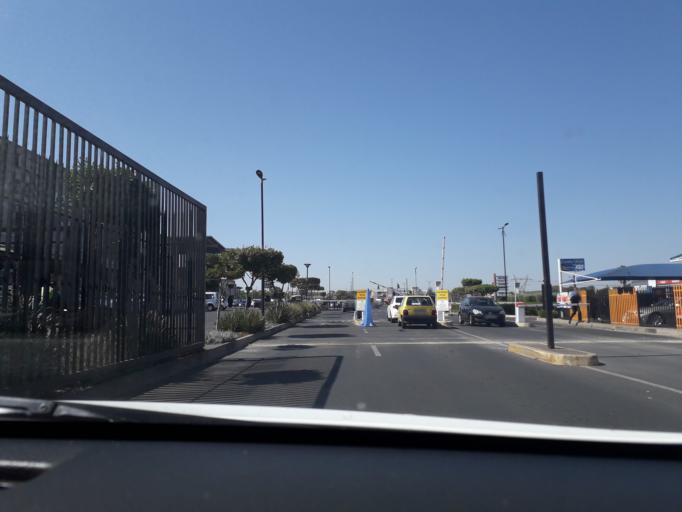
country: ZA
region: Gauteng
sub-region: City of Johannesburg Metropolitan Municipality
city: Modderfontein
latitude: -26.1046
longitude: 28.2223
